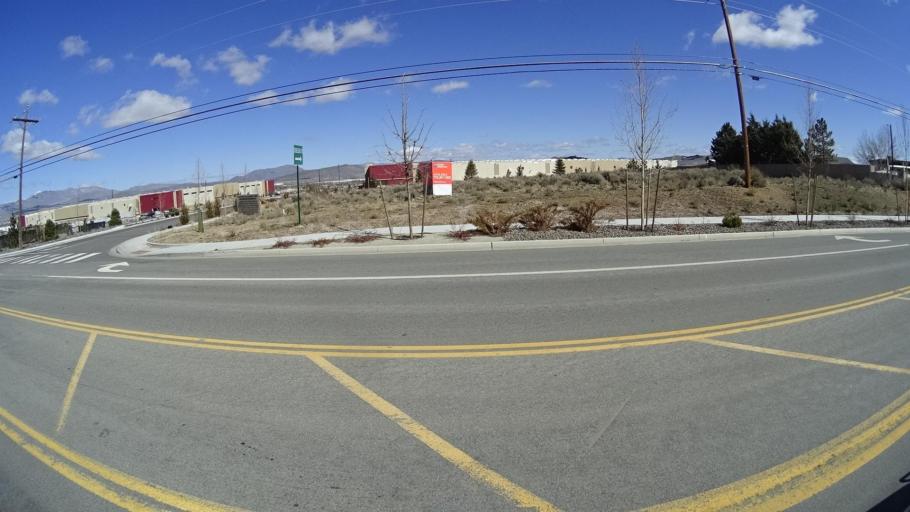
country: US
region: Nevada
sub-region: Washoe County
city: Lemmon Valley
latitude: 39.6112
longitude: -119.8704
